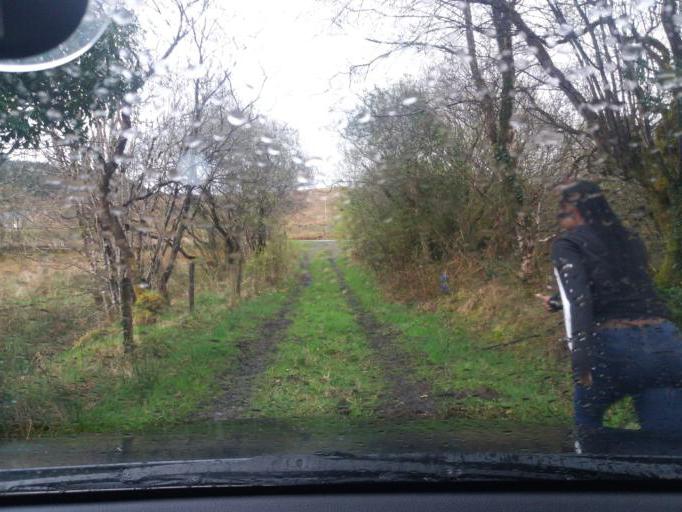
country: IE
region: Connaught
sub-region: County Leitrim
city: Manorhamilton
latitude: 54.2591
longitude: -7.9263
